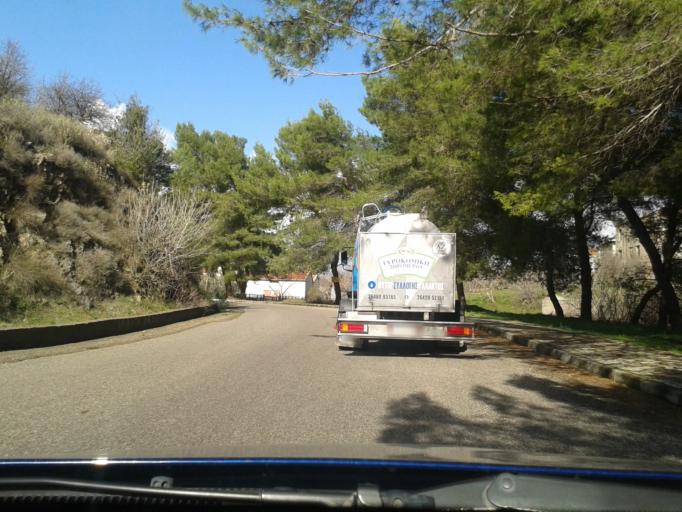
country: GR
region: West Greece
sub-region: Nomos Aitolias kai Akarnanias
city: Fitiai
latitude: 38.6916
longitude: 21.1842
